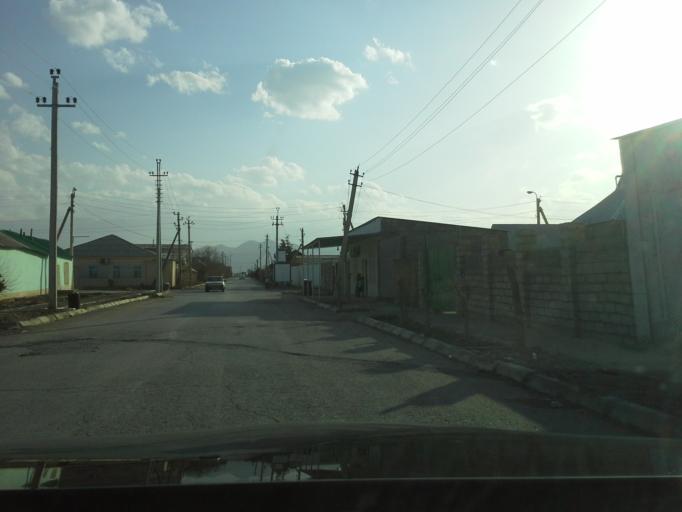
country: TM
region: Ahal
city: Abadan
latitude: 38.0201
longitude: 58.2314
